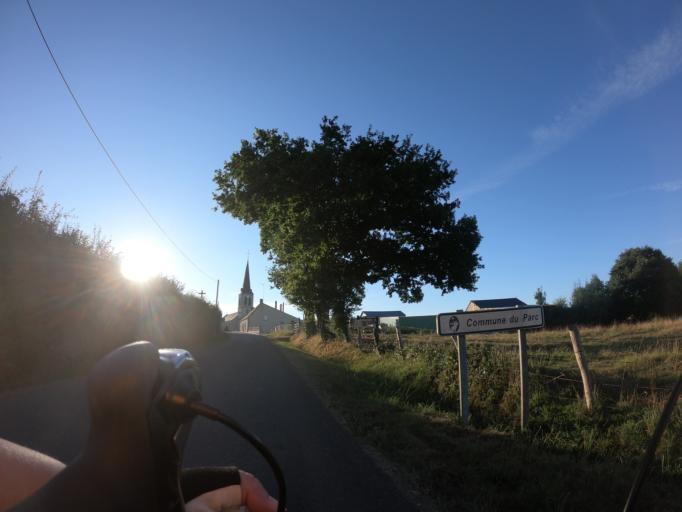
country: FR
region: Lower Normandy
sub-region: Departement de l'Orne
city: Magny-le-Desert
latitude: 48.5420
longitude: -0.3032
